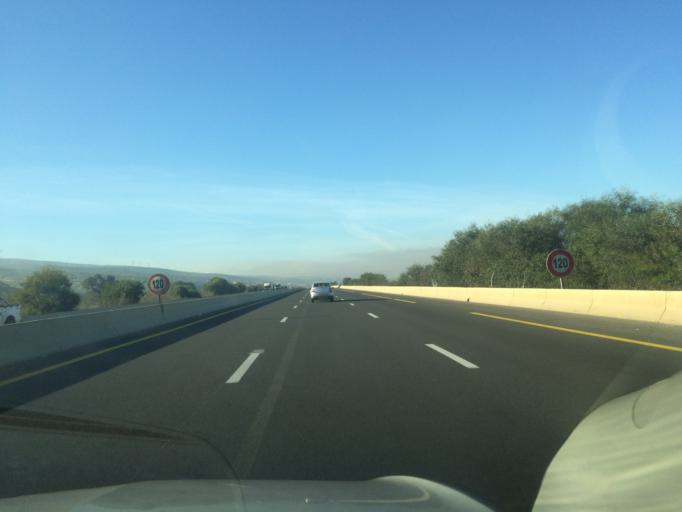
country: DZ
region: Relizane
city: Oued Rhiou
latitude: 36.0111
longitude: 1.0166
